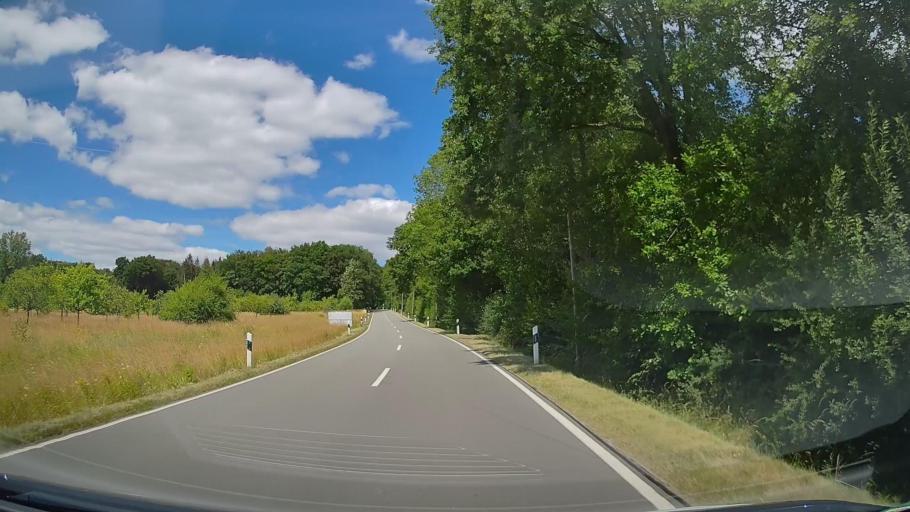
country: DE
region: Lower Saxony
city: Belm
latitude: 52.3551
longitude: 8.1445
